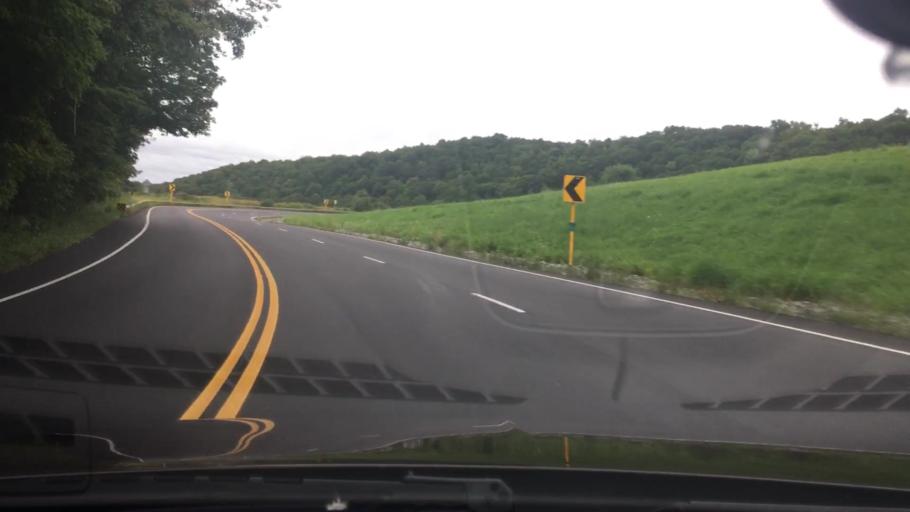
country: US
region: New York
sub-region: Dutchess County
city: Dover Plains
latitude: 41.8386
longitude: -73.5752
